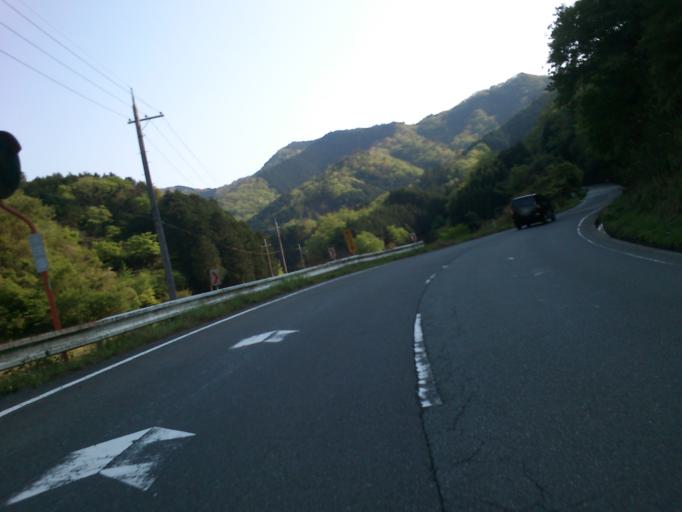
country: JP
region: Kyoto
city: Fukuchiyama
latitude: 35.2587
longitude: 135.0691
